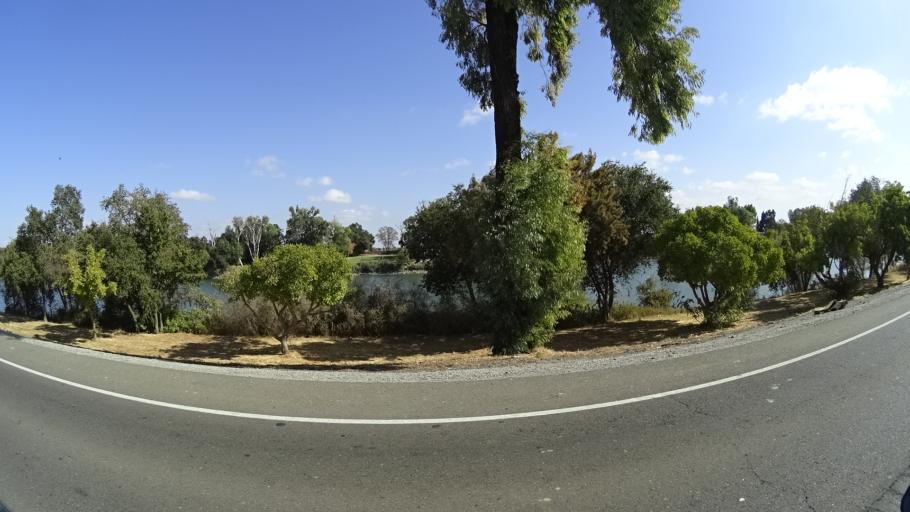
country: US
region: California
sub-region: Yolo County
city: West Sacramento
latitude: 38.6272
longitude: -121.5638
